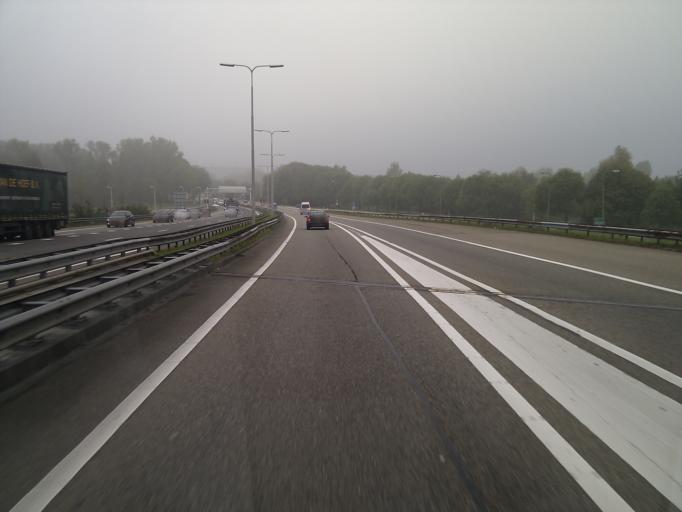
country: NL
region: Utrecht
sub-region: Gemeente Utrecht
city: Utrecht
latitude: 52.1197
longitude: 5.1410
